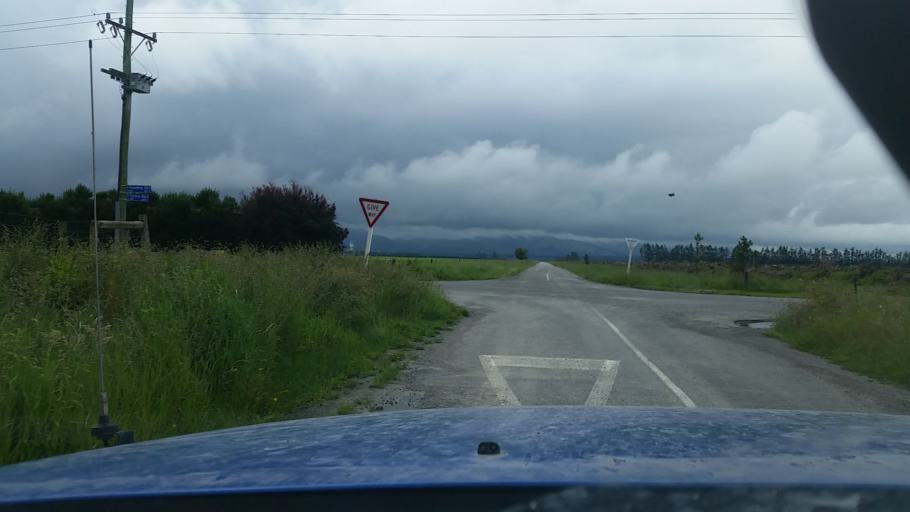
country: NZ
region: Canterbury
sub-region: Ashburton District
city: Methven
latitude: -43.7185
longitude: 171.4574
